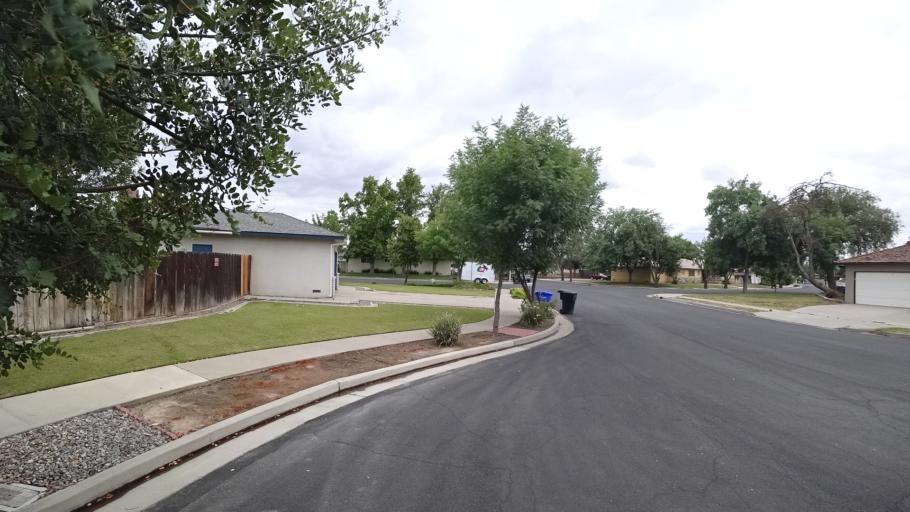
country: US
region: California
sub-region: Kings County
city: Hanford
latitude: 36.3373
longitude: -119.6603
